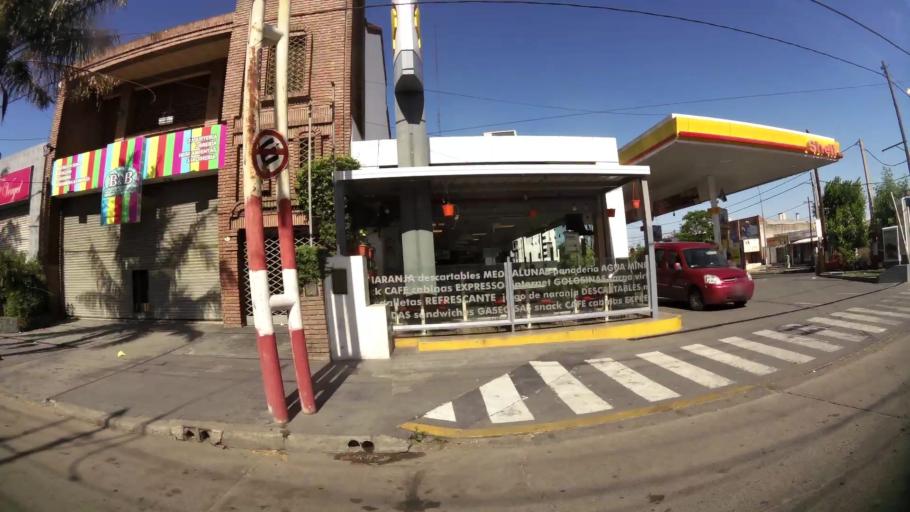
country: AR
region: Cordoba
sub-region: Departamento de Capital
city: Cordoba
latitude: -31.3698
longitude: -64.1839
